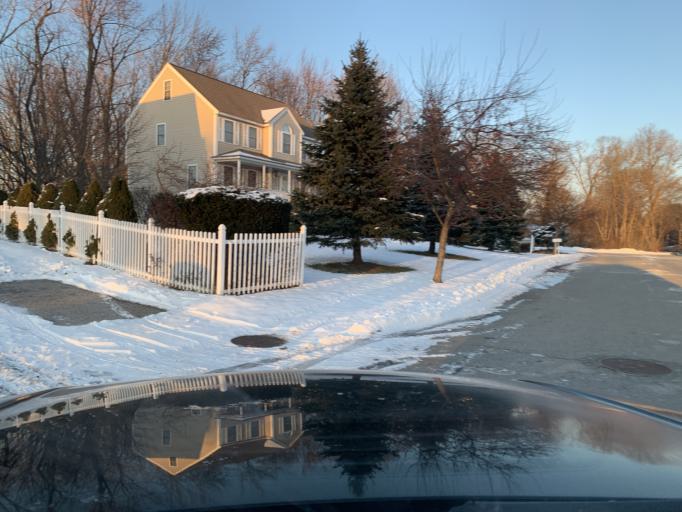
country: US
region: Massachusetts
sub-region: Essex County
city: Haverhill
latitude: 42.7898
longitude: -71.1137
